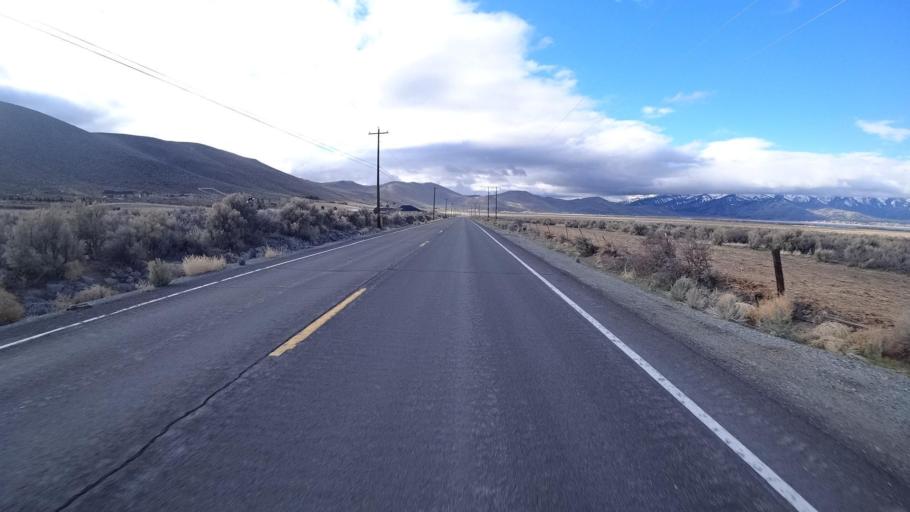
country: US
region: Nevada
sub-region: Carson City
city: Carson City
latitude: 39.2712
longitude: -119.7566
